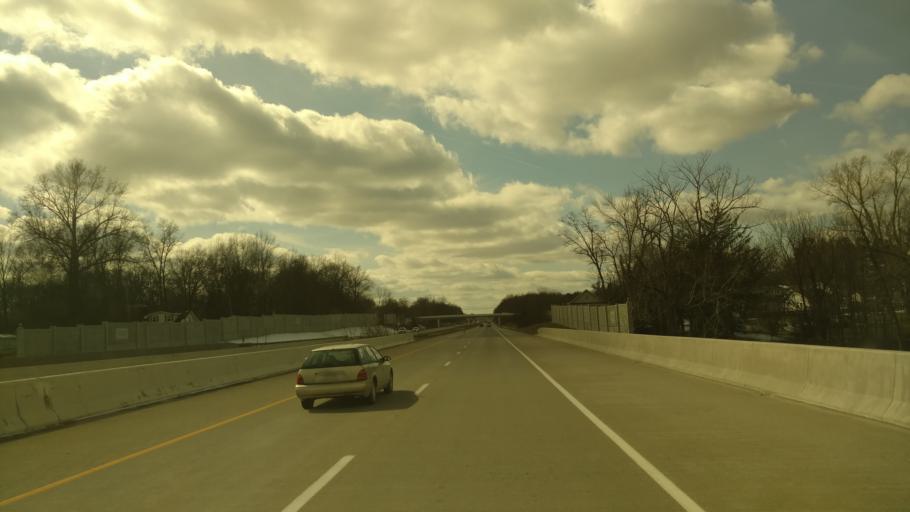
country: US
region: Ohio
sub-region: Mahoning County
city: Craig Beach
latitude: 41.1003
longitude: -80.9838
